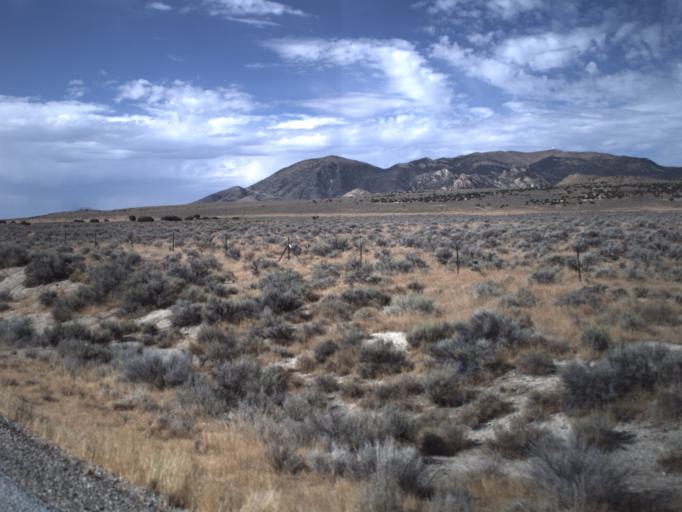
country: US
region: Utah
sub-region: Tooele County
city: Wendover
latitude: 41.5293
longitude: -113.5943
